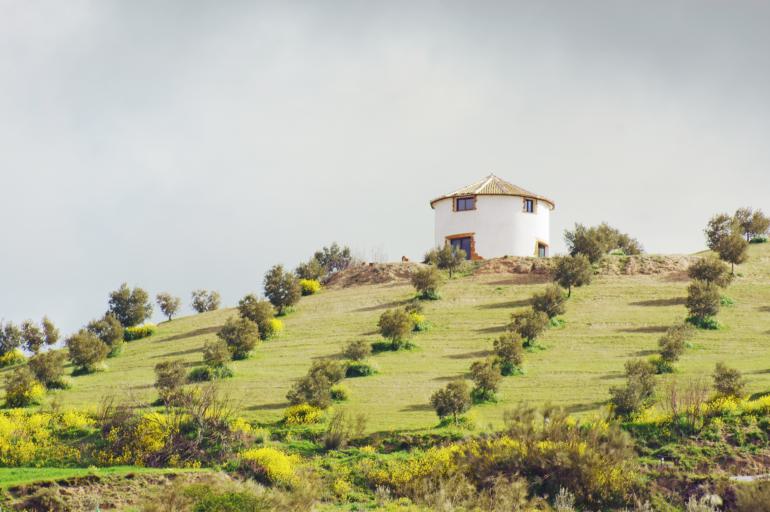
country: ES
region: Andalusia
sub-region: Provincia de Granada
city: Alhama de Granada
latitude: 37.0775
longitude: -3.9807
